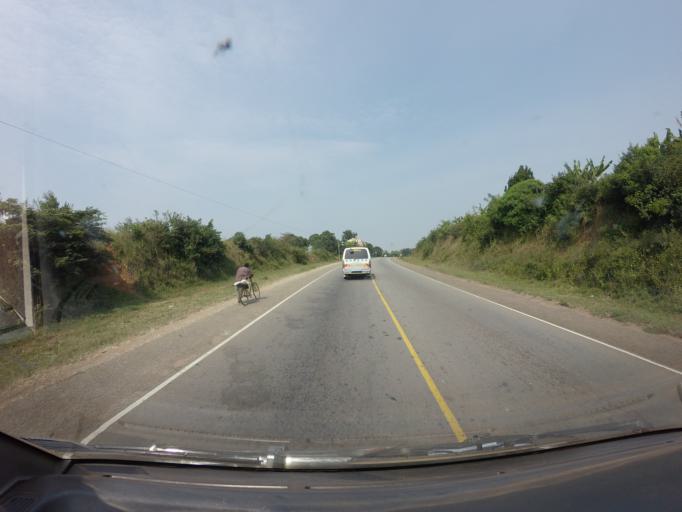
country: UG
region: Central Region
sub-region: Lwengo District
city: Lwengo
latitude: -0.3960
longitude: 31.4199
